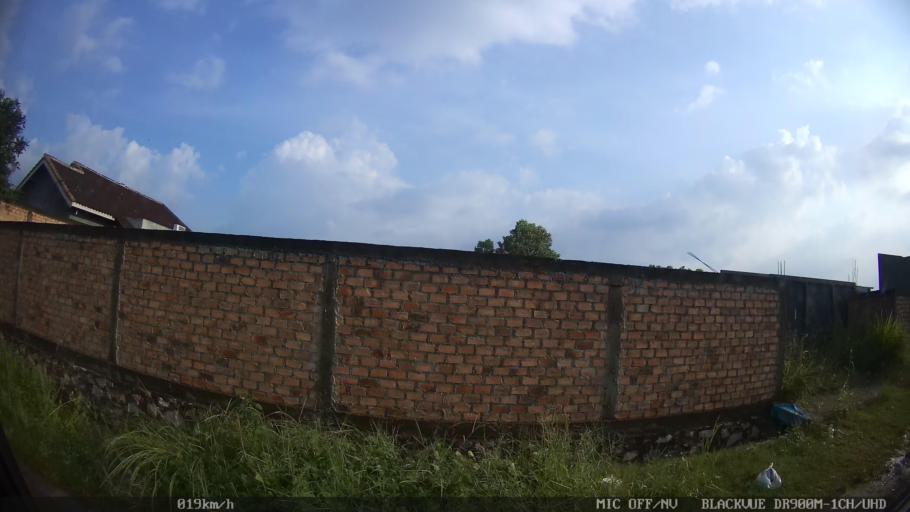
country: ID
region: Lampung
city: Kedaton
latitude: -5.3911
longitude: 105.3129
